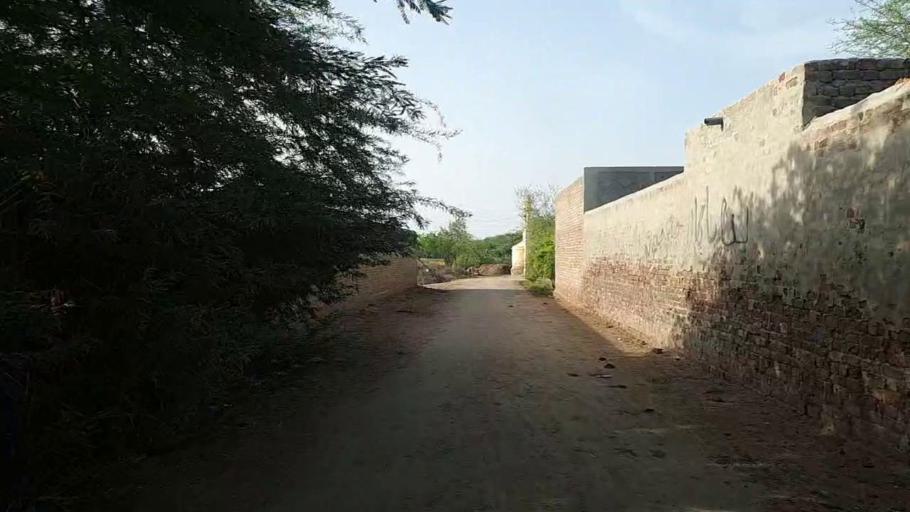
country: PK
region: Sindh
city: Karaundi
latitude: 26.8923
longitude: 68.3087
